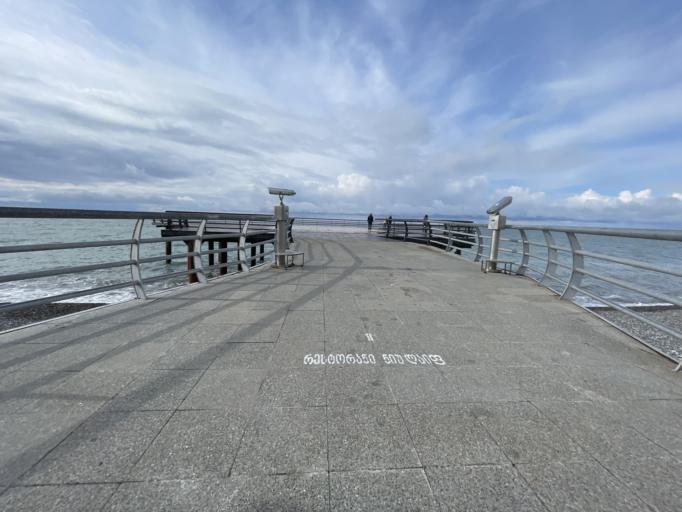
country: GE
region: Ajaria
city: Batumi
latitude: 41.6562
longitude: 41.6334
